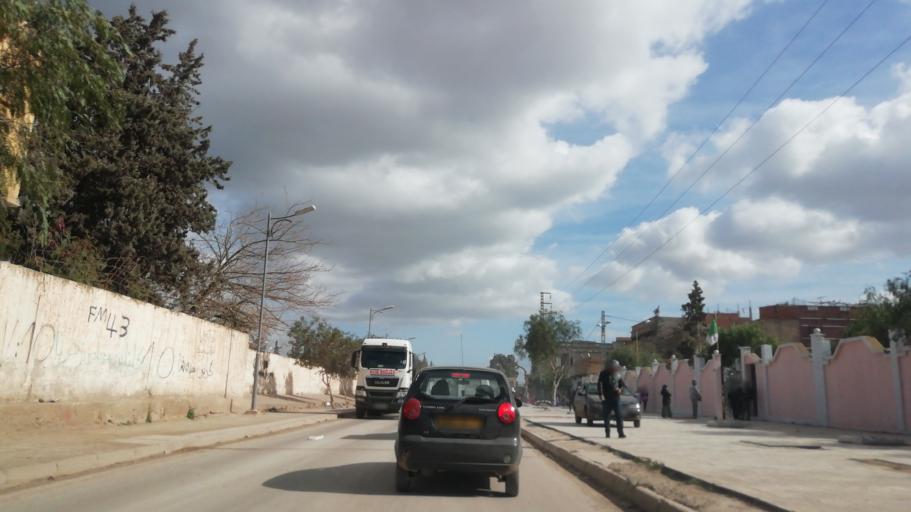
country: DZ
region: Oran
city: Es Senia
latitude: 35.6521
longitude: -0.5733
